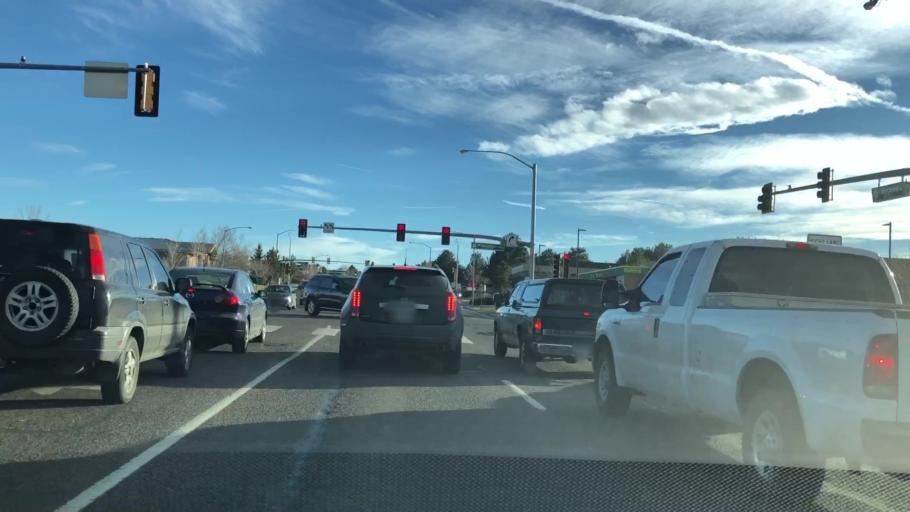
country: US
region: Colorado
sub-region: Adams County
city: Aurora
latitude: 39.6970
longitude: -104.7912
